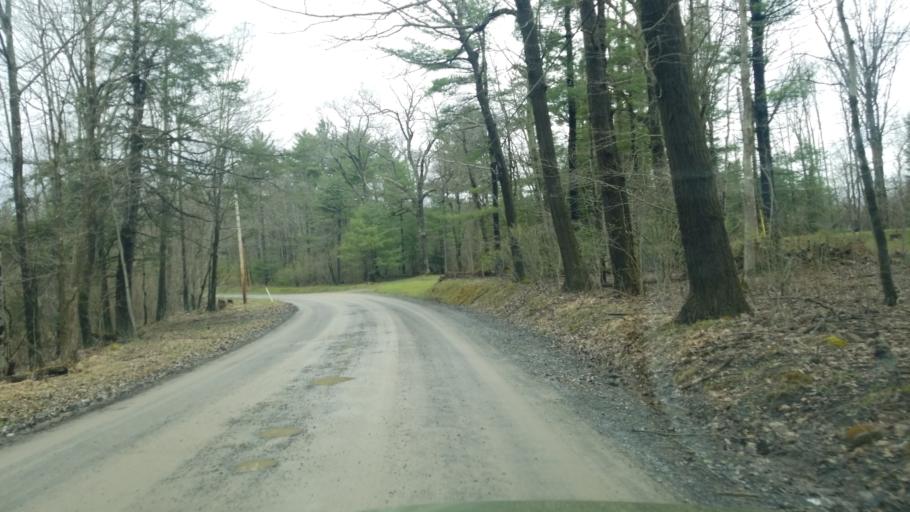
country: US
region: Pennsylvania
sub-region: Clearfield County
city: Shiloh
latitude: 41.1402
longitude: -78.3329
